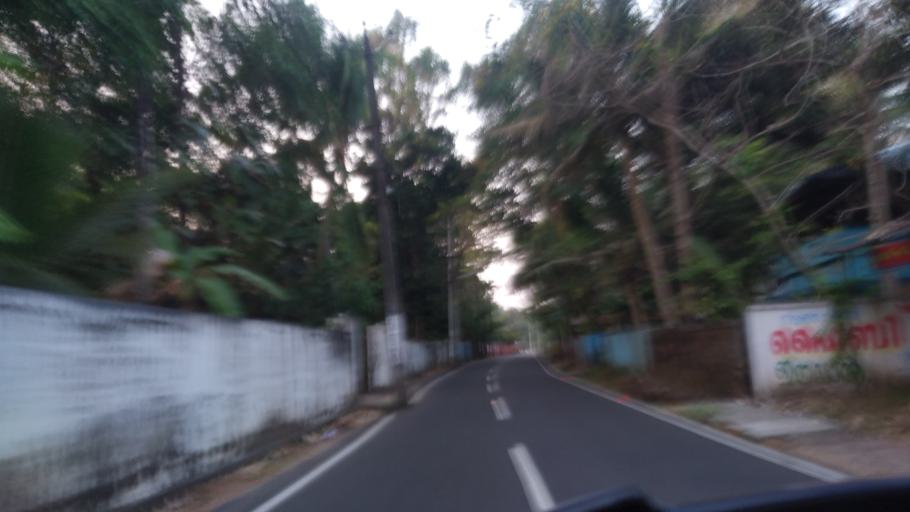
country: IN
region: Kerala
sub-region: Ernakulam
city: Elur
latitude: 10.1082
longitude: 76.2454
